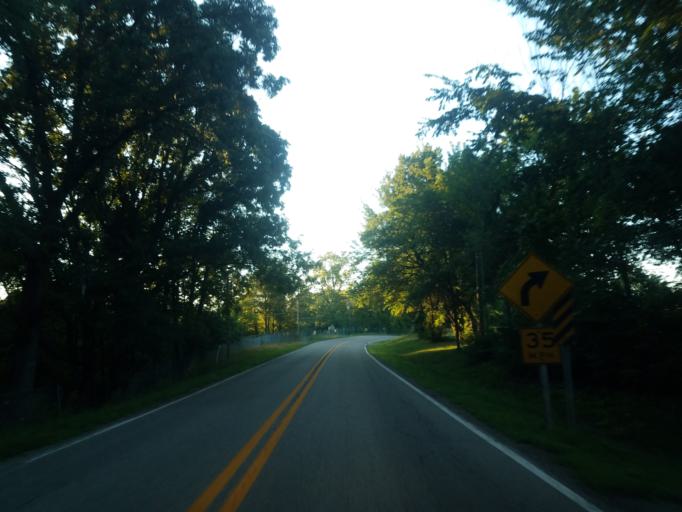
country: US
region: Illinois
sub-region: McLean County
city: Bloomington
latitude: 40.4602
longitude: -89.0352
